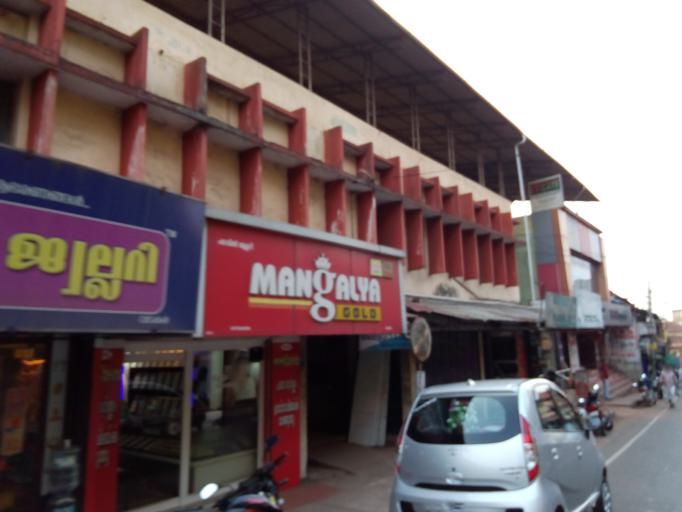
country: IN
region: Kerala
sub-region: Kozhikode
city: Badagara
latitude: 11.5989
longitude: 75.5863
